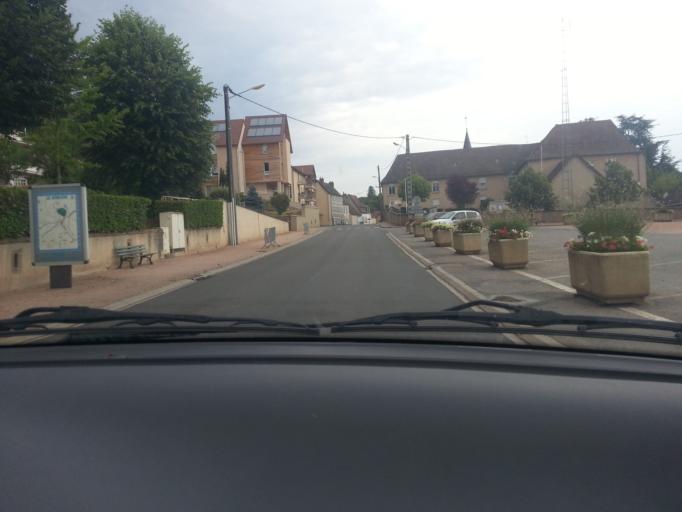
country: FR
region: Auvergne
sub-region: Departement de l'Allier
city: Le Donjon
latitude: 46.3485
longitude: 3.7932
